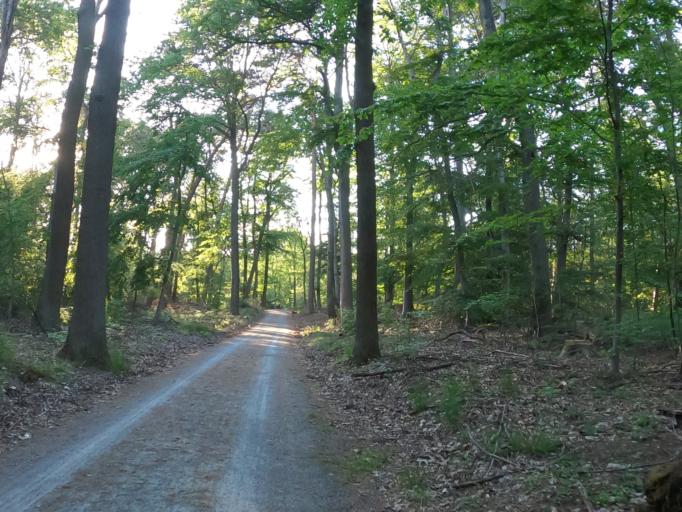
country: DE
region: Hesse
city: Niederrad
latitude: 50.0598
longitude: 8.5845
